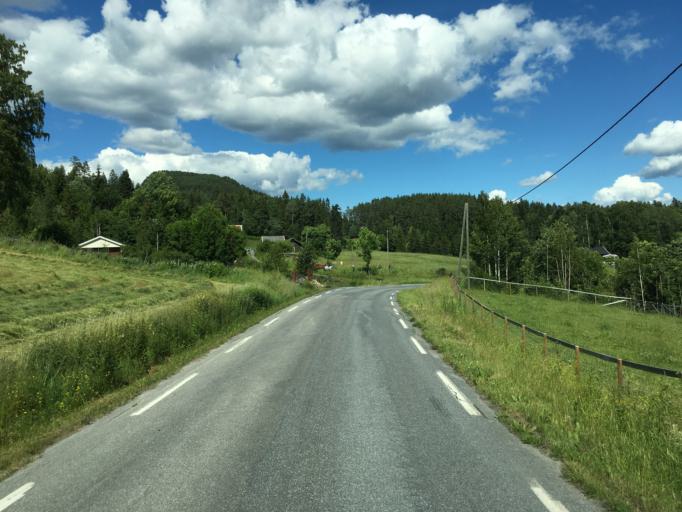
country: NO
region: Oppland
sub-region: Jevnaker
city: Jevnaker
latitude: 60.3353
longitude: 10.3436
